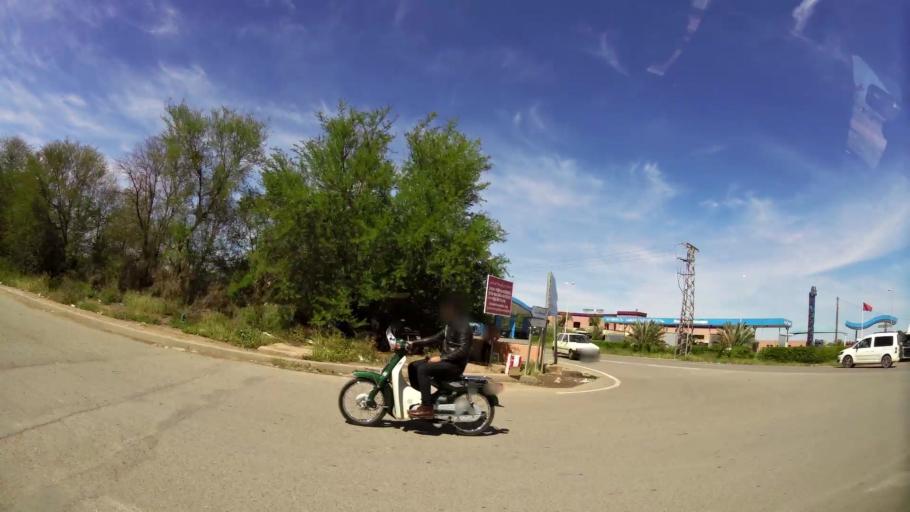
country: MA
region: Marrakech-Tensift-Al Haouz
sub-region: Marrakech
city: Marrakesh
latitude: 31.6411
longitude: -8.1056
